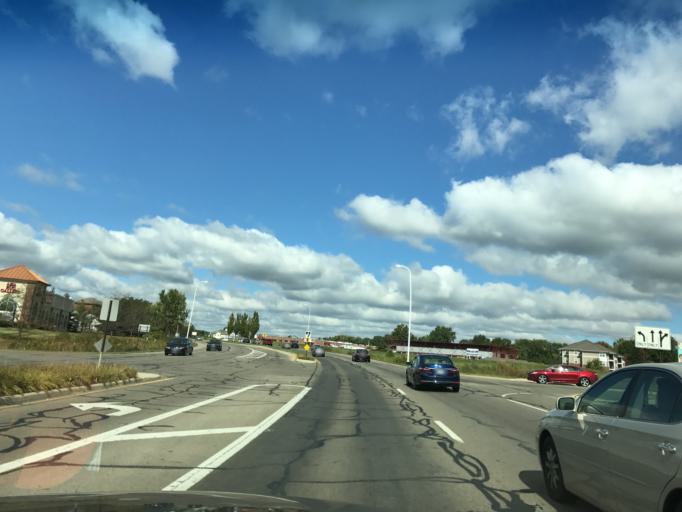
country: US
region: Ohio
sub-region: Delaware County
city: Lewis Center
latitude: 40.1481
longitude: -82.9930
